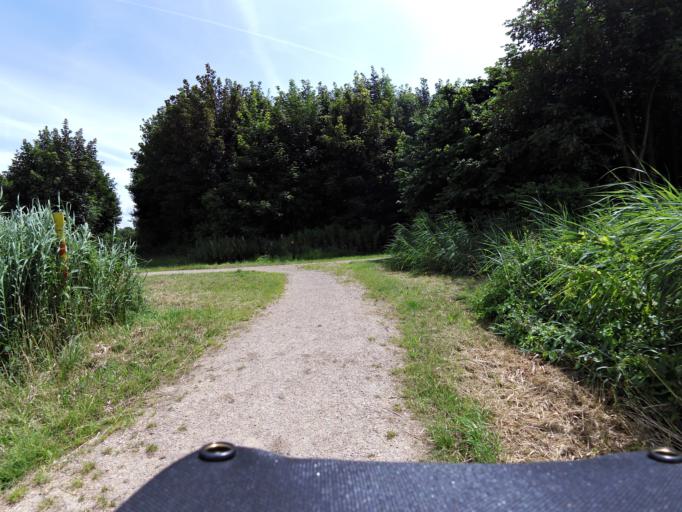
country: NL
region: South Holland
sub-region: Gemeente Albrandswaard
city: Rhoon
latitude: 51.8654
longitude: 4.4144
